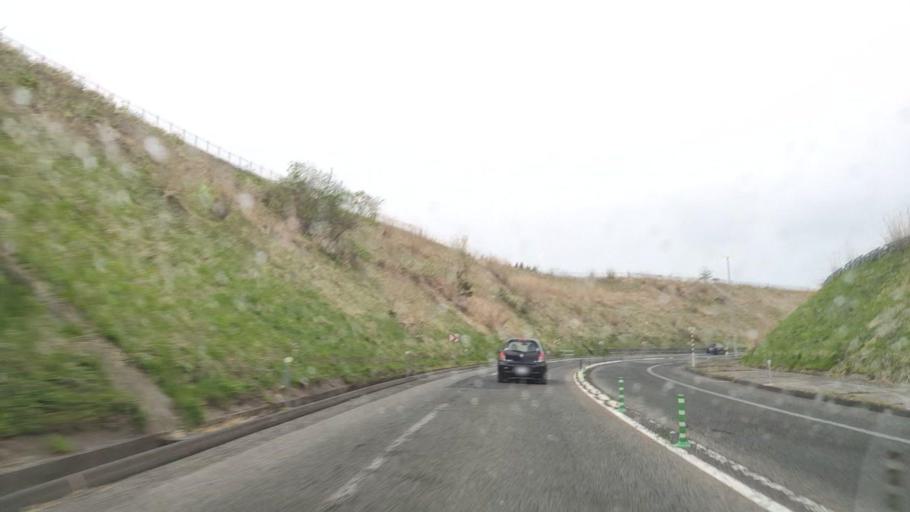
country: JP
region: Akita
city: Noshiromachi
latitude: 40.2088
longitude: 140.1926
